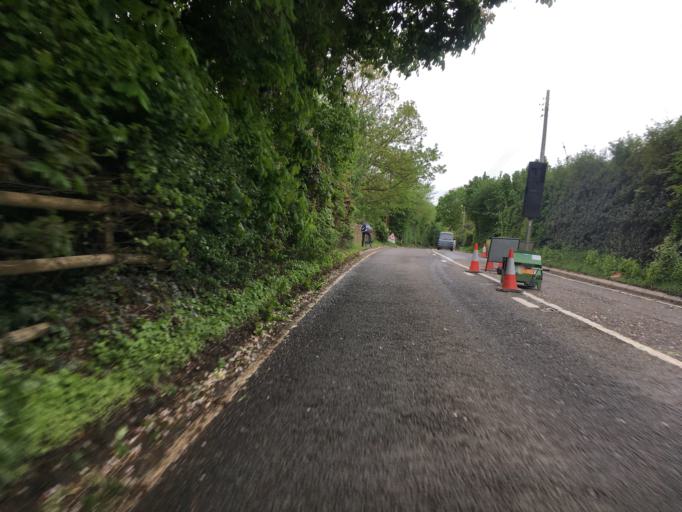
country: GB
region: England
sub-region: North Somerset
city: Sandford
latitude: 51.3314
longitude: -2.8453
